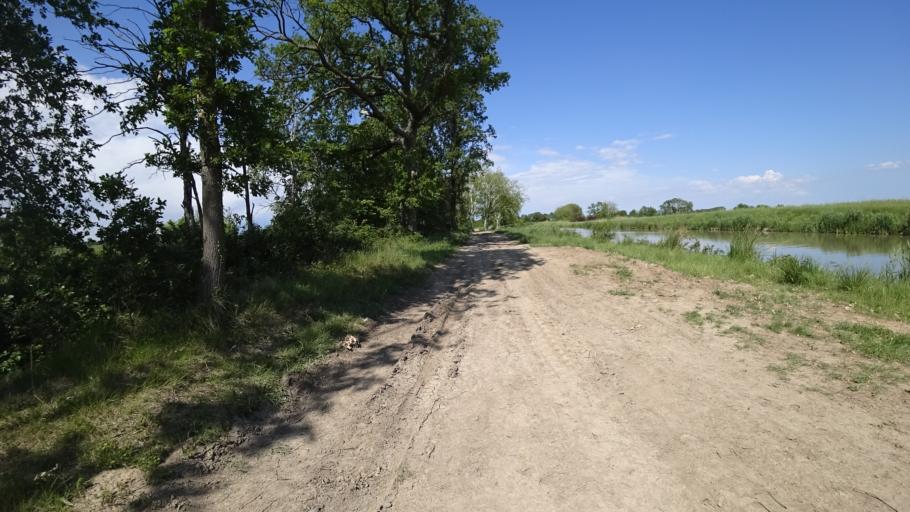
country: FR
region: Languedoc-Roussillon
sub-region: Departement de l'Aude
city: Ginestas
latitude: 43.2514
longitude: 2.8801
